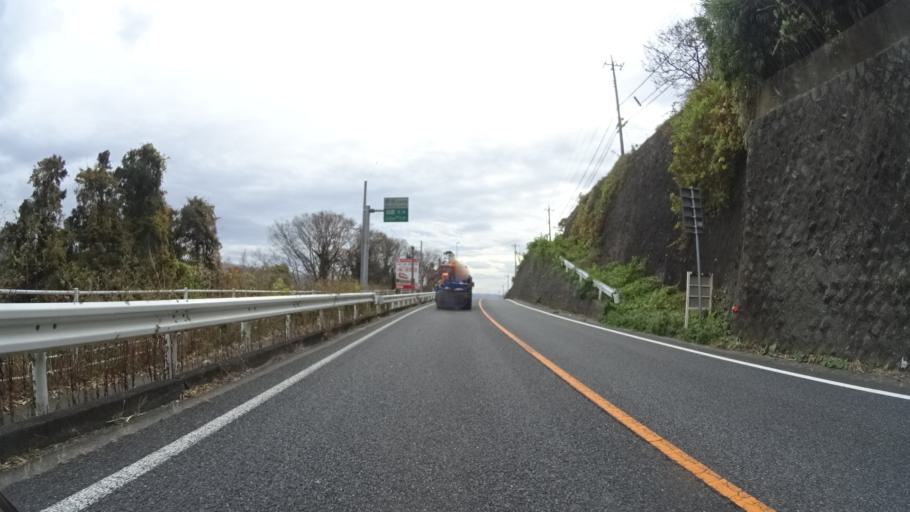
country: JP
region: Gunma
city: Numata
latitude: 36.5635
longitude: 139.0379
